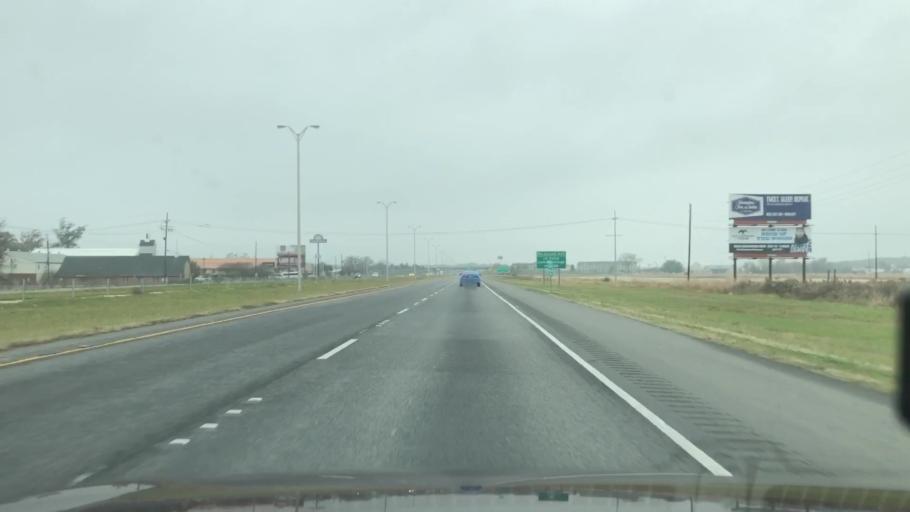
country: US
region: Louisiana
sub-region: Ouachita Parish
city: Lakeshore
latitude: 32.4938
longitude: -92.0452
